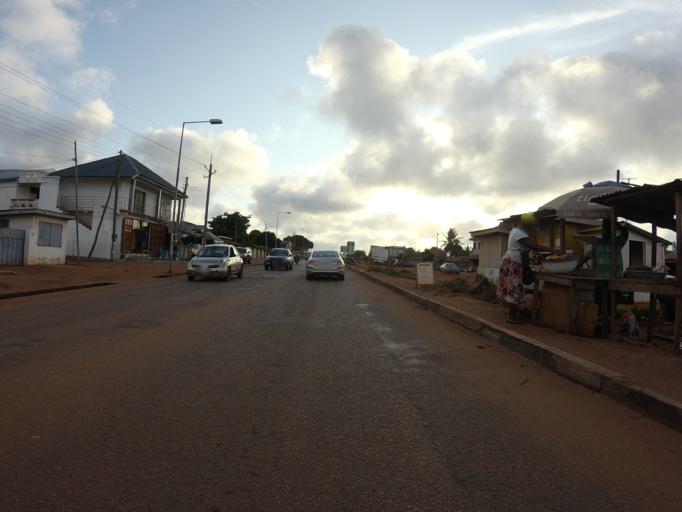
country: GH
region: Greater Accra
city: Teshi Old Town
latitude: 5.6089
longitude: -0.1091
